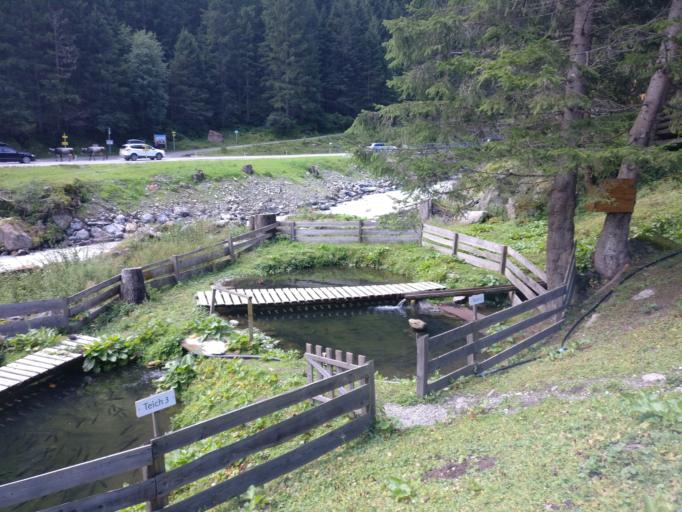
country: AT
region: Tyrol
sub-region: Politischer Bezirk Innsbruck Land
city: Neustift im Stubaital
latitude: 47.0233
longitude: 11.2134
